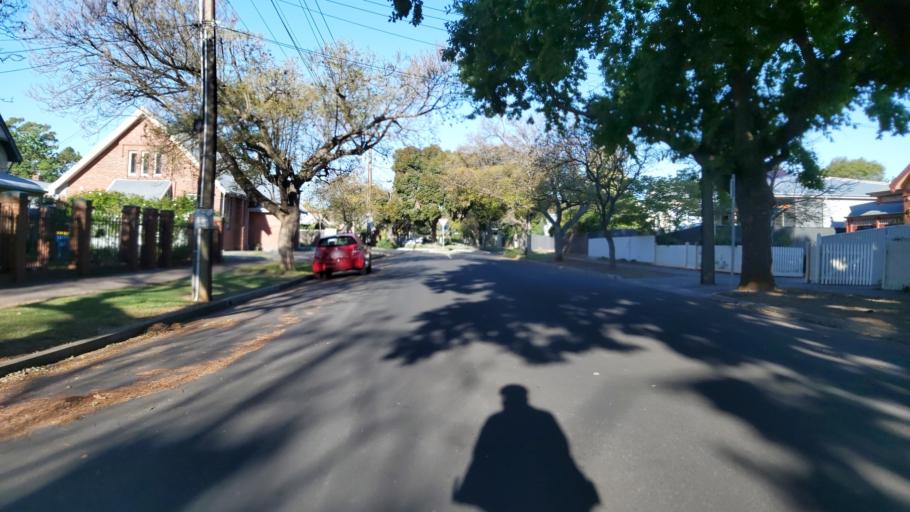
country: AU
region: South Australia
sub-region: Unley
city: Unley
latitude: -34.9452
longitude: 138.5956
